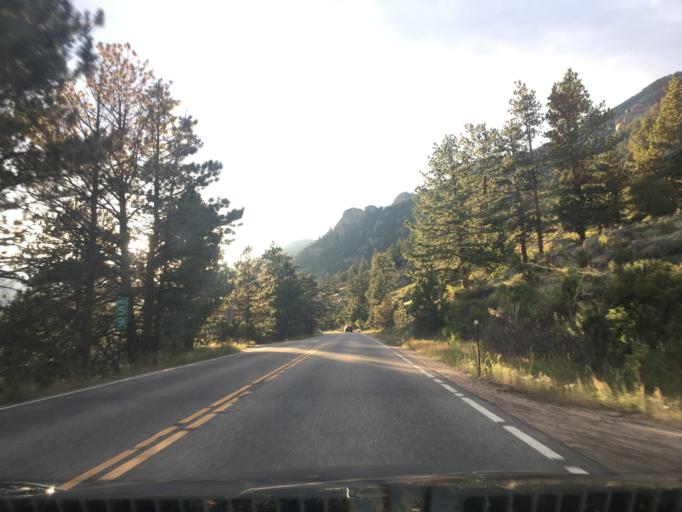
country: US
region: Colorado
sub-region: Larimer County
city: Estes Park
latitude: 40.3978
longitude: -105.5675
